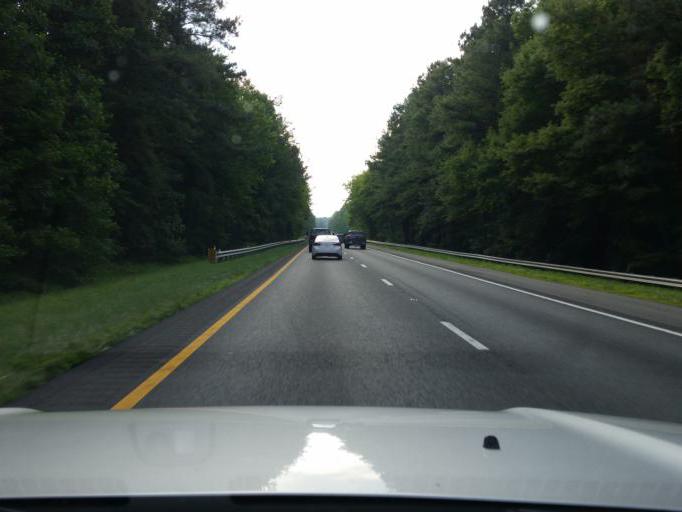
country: US
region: Virginia
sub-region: New Kent County
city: New Kent
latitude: 37.4703
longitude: -76.9002
